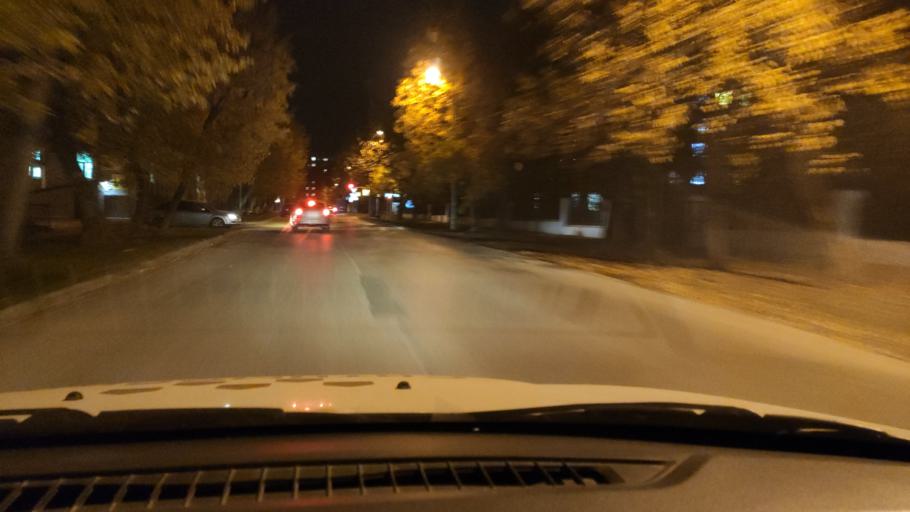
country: RU
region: Perm
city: Perm
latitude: 58.0201
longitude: 56.2831
